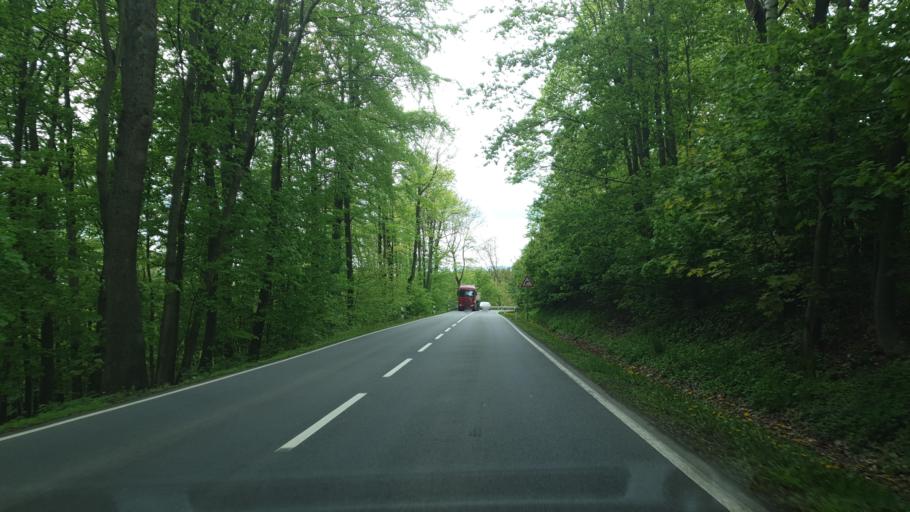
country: DE
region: Saxony
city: Hartenstein
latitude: 50.6574
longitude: 12.6906
